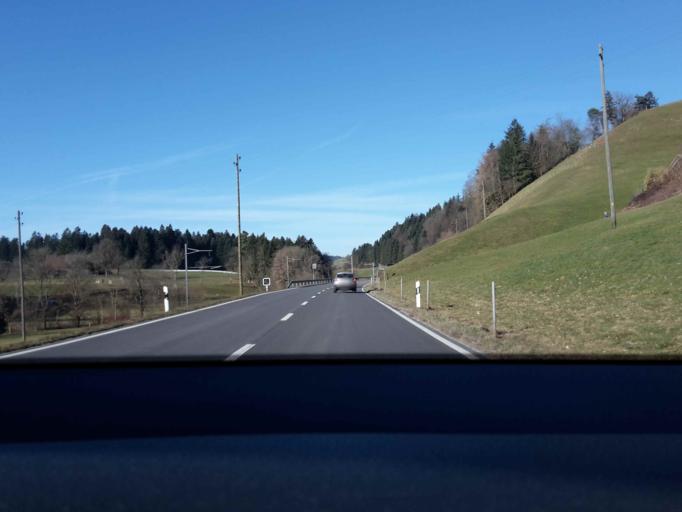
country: CH
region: Bern
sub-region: Emmental District
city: Durrenroth
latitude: 47.0919
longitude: 7.7871
